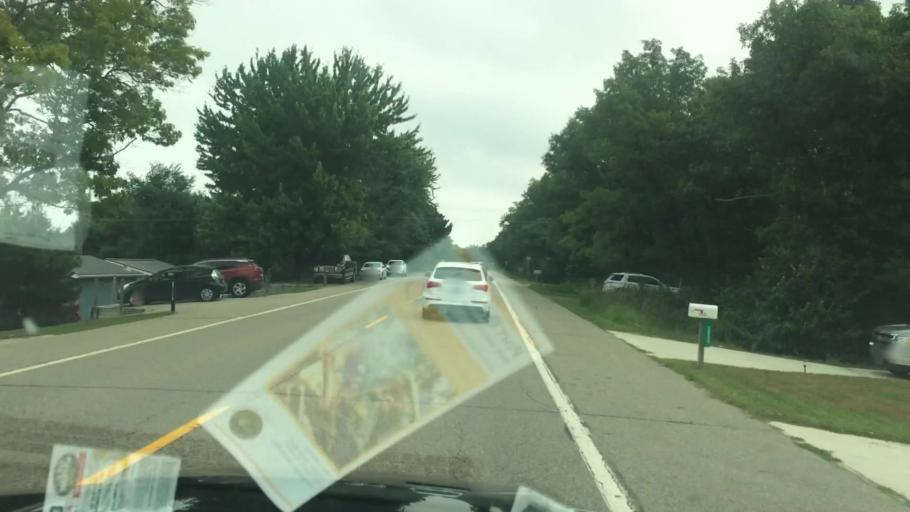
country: US
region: Michigan
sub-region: Huron County
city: Pigeon
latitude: 43.9863
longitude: -83.1594
